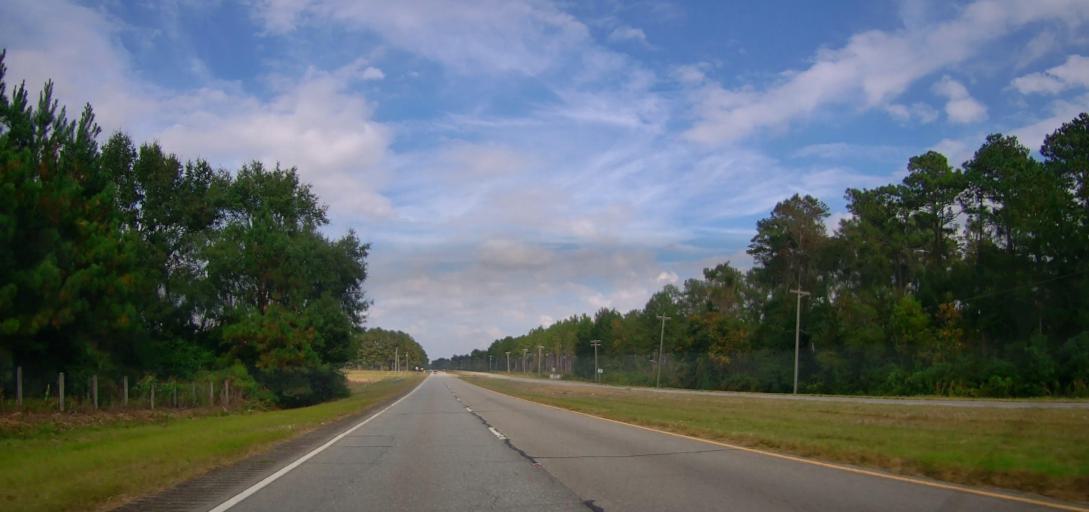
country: US
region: Georgia
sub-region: Thomas County
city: Thomasville
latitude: 30.7927
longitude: -84.0309
